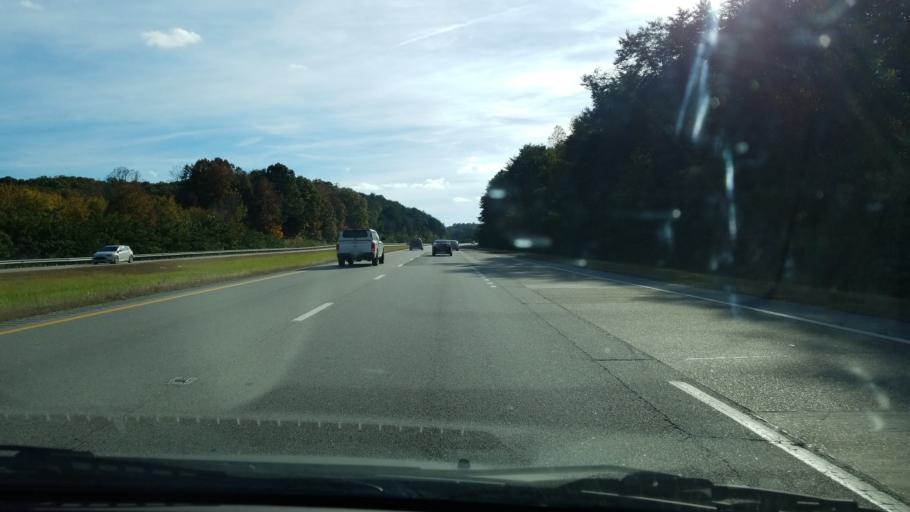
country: US
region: Tennessee
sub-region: Hamilton County
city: Soddy-Daisy
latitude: 35.2721
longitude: -85.1583
